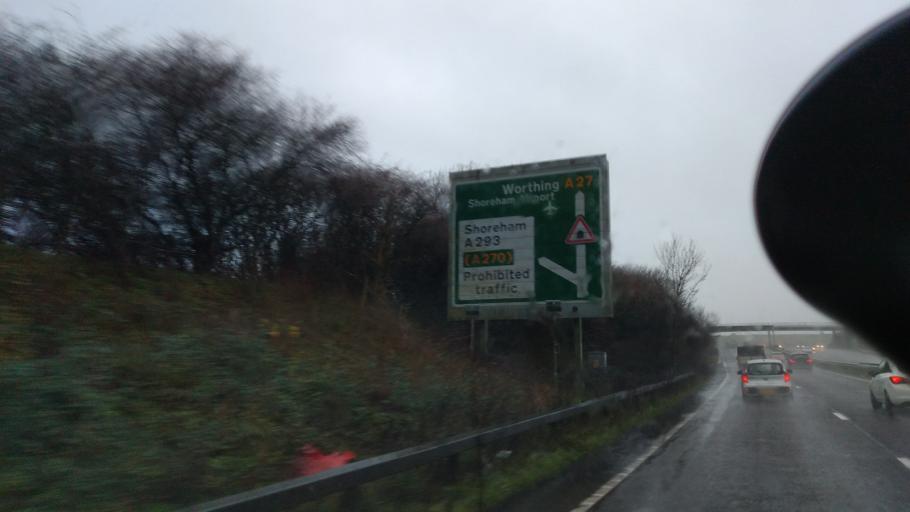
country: GB
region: England
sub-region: East Sussex
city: Portslade
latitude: 50.8553
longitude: -0.2036
